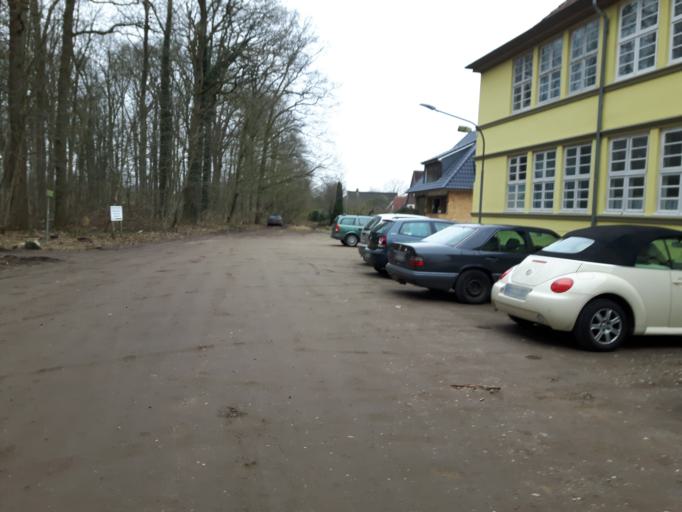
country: DE
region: Schleswig-Holstein
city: Bordesholm
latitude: 54.1768
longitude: 10.0066
